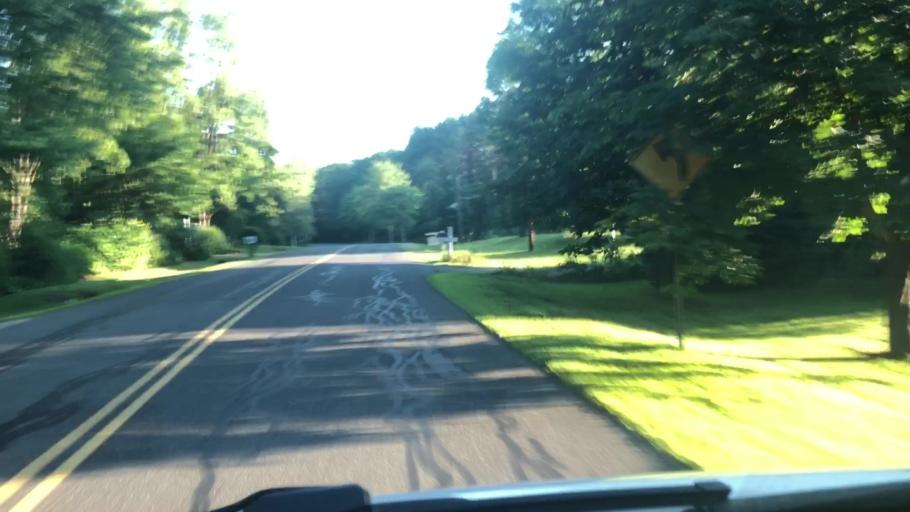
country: US
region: Massachusetts
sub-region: Hampshire County
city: Williamsburg
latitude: 42.3657
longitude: -72.7243
